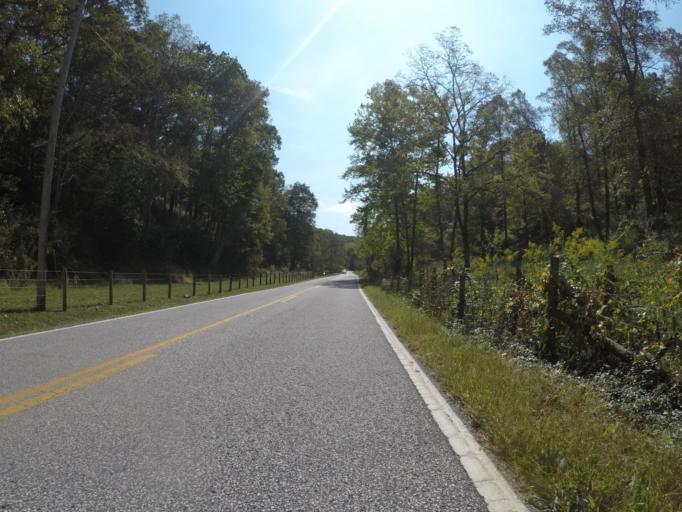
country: US
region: West Virginia
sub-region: Cabell County
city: Lesage
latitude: 38.5777
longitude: -82.4095
